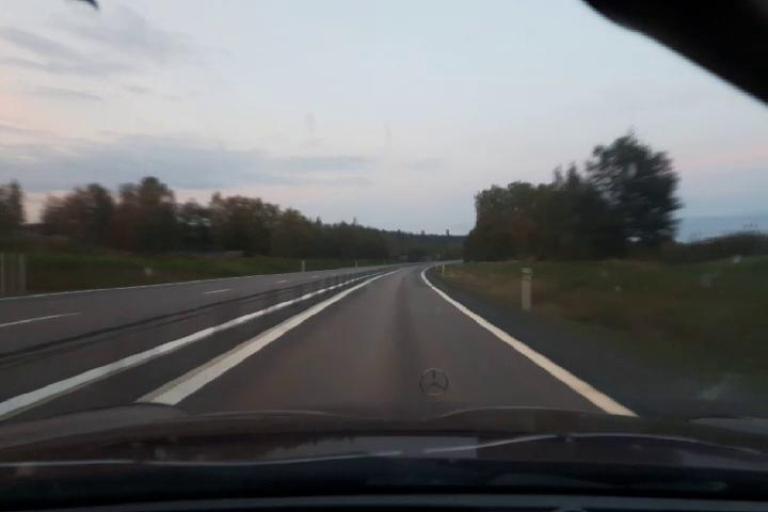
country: SE
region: Vaesternorrland
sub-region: Kramfors Kommun
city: Nordingra
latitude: 62.8752
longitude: 18.0562
